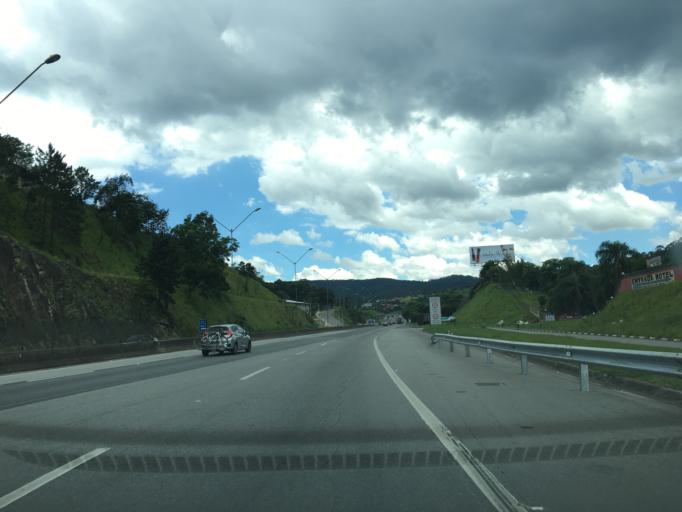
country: BR
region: Sao Paulo
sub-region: Mairipora
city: Mairipora
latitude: -23.3331
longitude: -46.5766
